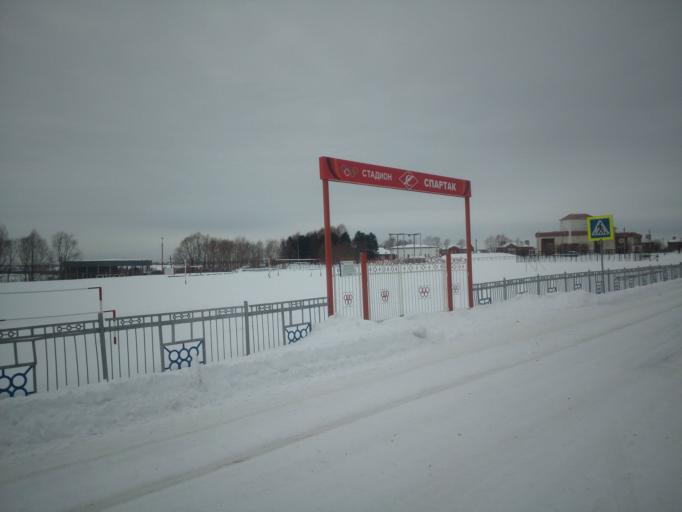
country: RU
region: Bashkortostan
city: Kaltasy
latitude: 55.8070
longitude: 54.5319
